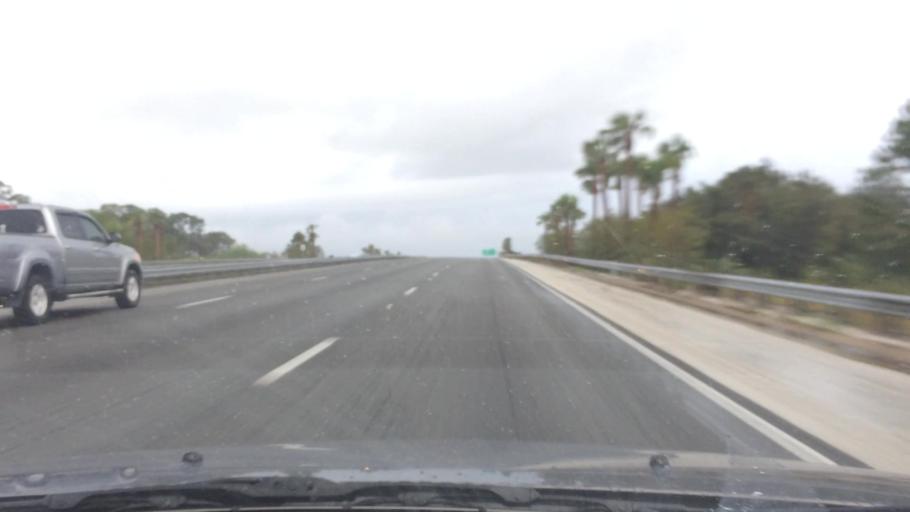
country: US
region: Florida
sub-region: Volusia County
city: Ormond-by-the-Sea
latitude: 29.3309
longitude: -81.1311
